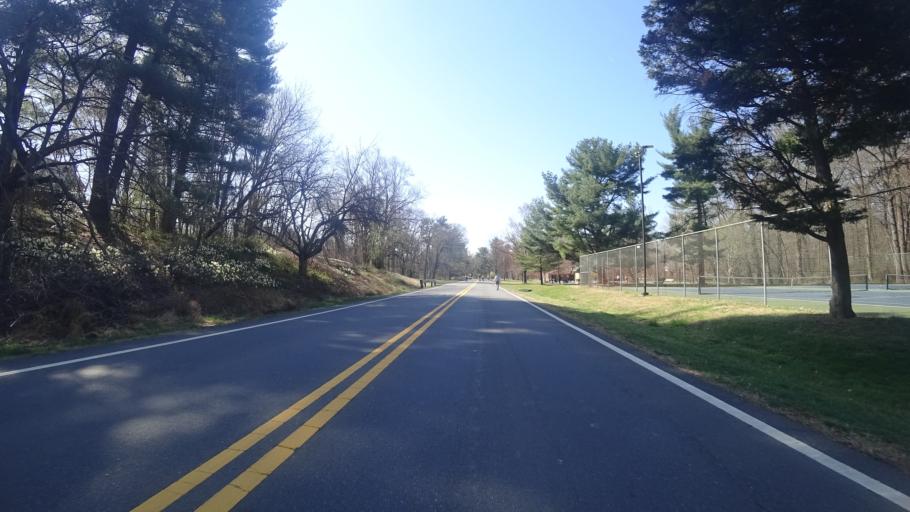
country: US
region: Maryland
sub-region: Montgomery County
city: Kemp Mill
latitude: 39.0270
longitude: -77.0289
